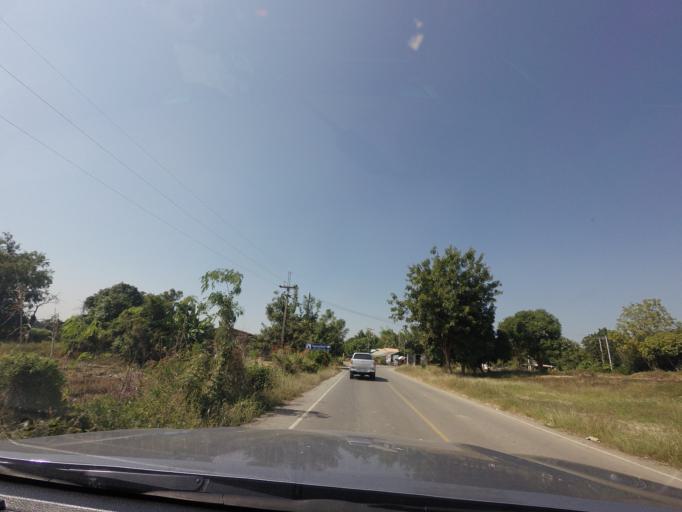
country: TH
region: Sukhothai
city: Si Samrong
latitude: 17.1314
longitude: 99.7783
